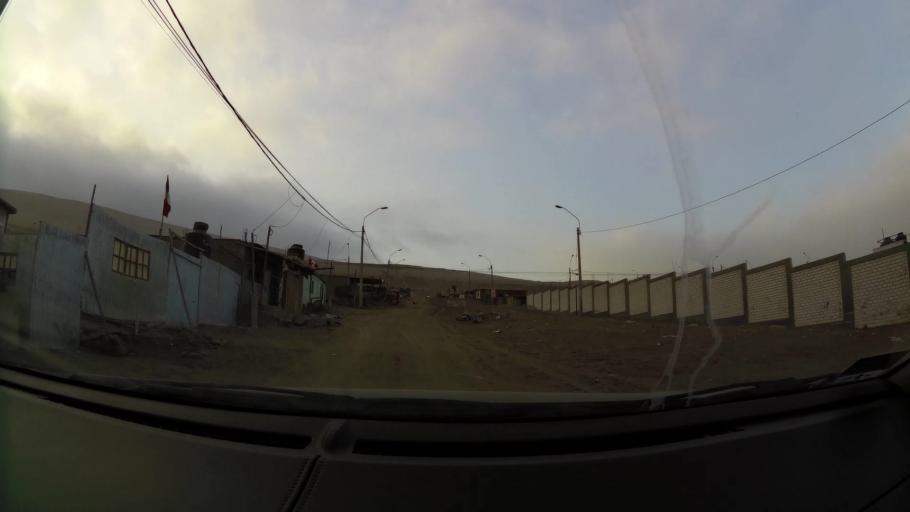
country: PE
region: Lima
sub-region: Lima
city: Santa Rosa
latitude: -11.7301
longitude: -77.1429
